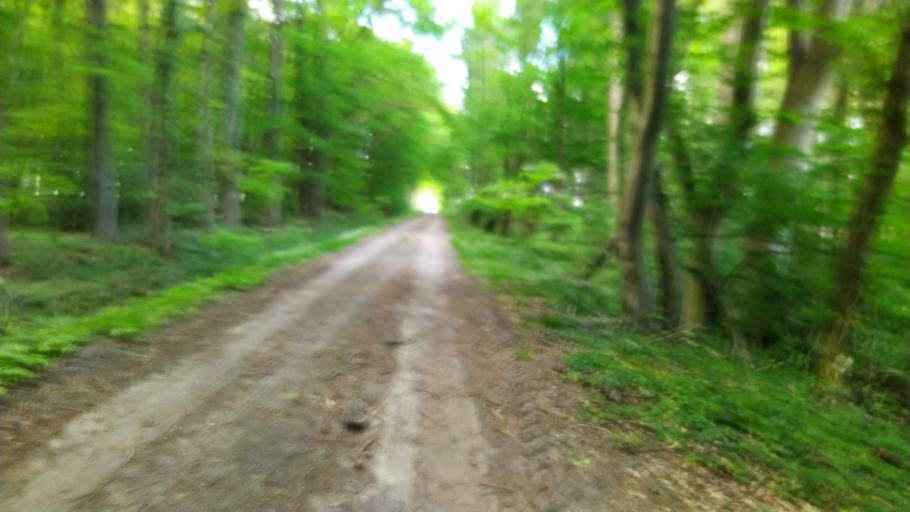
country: DE
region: Lower Saxony
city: Brest
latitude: 53.4166
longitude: 9.3835
